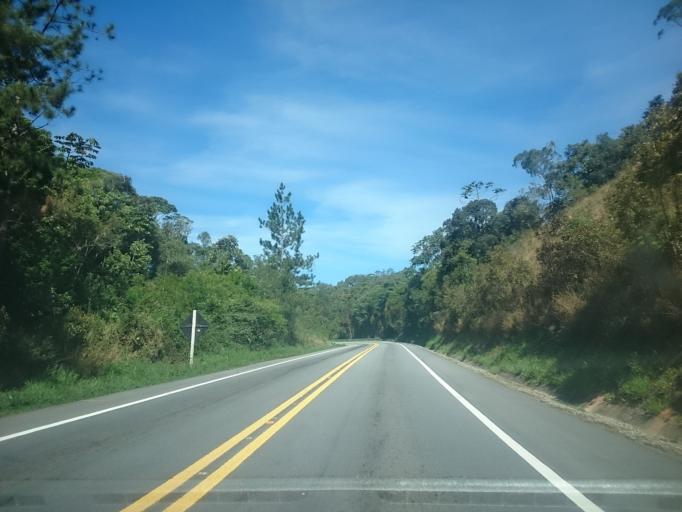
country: BR
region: Santa Catarina
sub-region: Santo Amaro Da Imperatriz
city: Santo Amaro da Imperatriz
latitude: -27.7053
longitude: -48.9554
